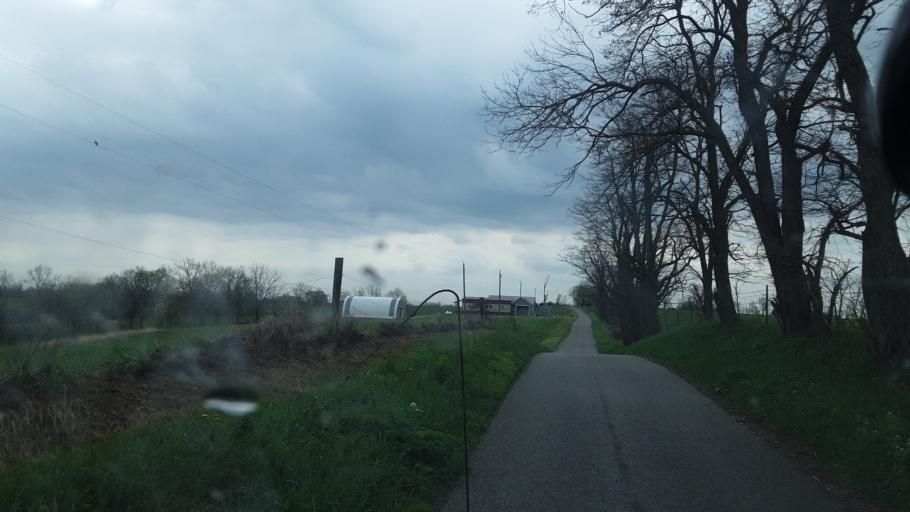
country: US
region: Kentucky
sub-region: Owen County
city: Owenton
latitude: 38.6096
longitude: -84.7695
